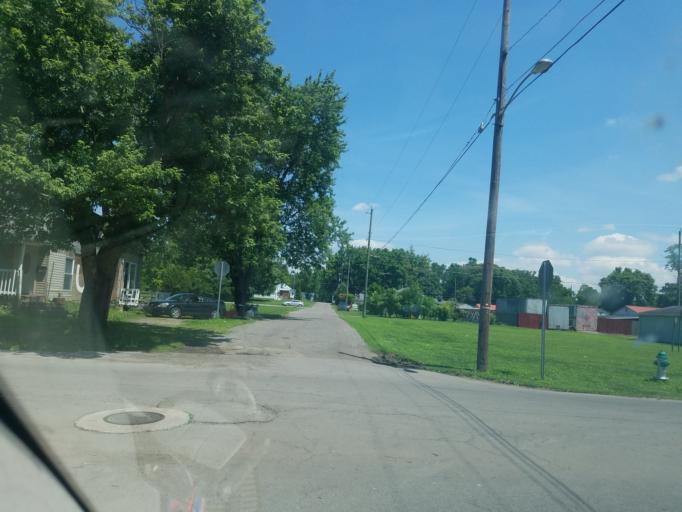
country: US
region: Ohio
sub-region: Hardin County
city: Kenton
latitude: 40.6413
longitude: -83.6190
